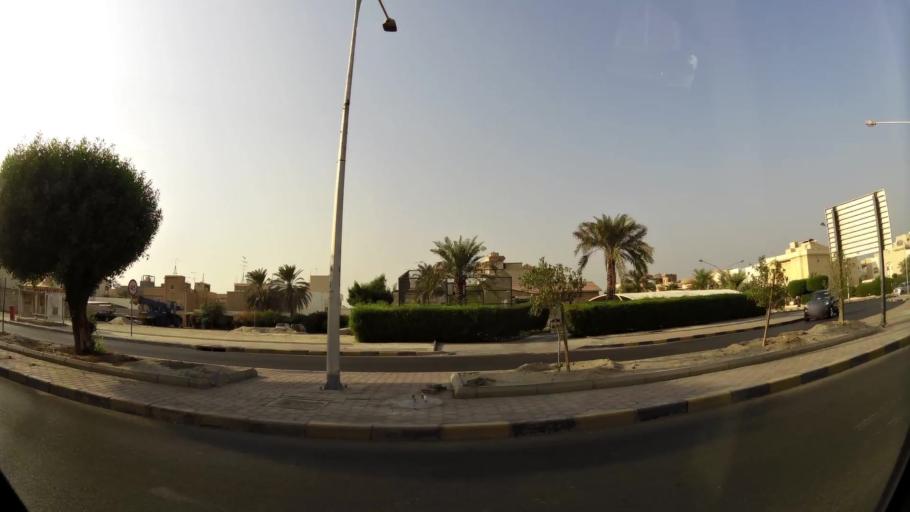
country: KW
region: Muhafazat Hawalli
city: Hawalli
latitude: 29.3148
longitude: 48.0098
